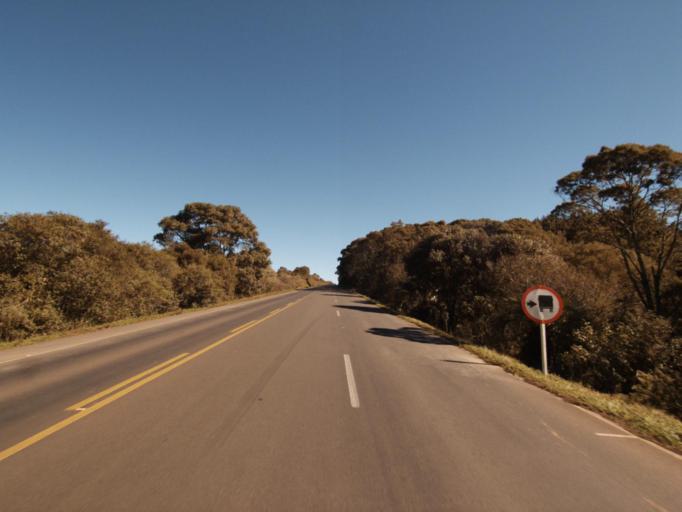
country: BR
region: Santa Catarina
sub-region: Concordia
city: Concordia
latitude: -26.9196
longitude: -51.9344
